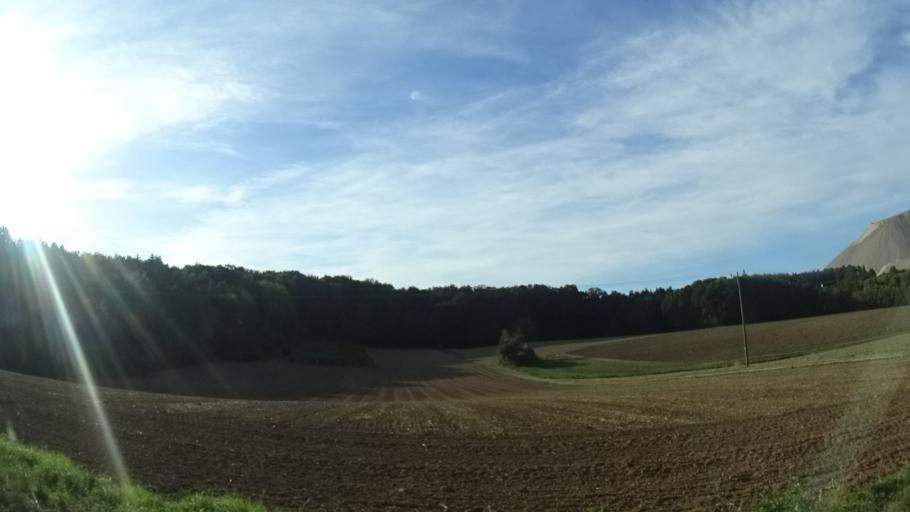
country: DE
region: Hesse
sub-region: Regierungsbezirk Kassel
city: Neuhof
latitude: 50.4560
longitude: 9.5935
